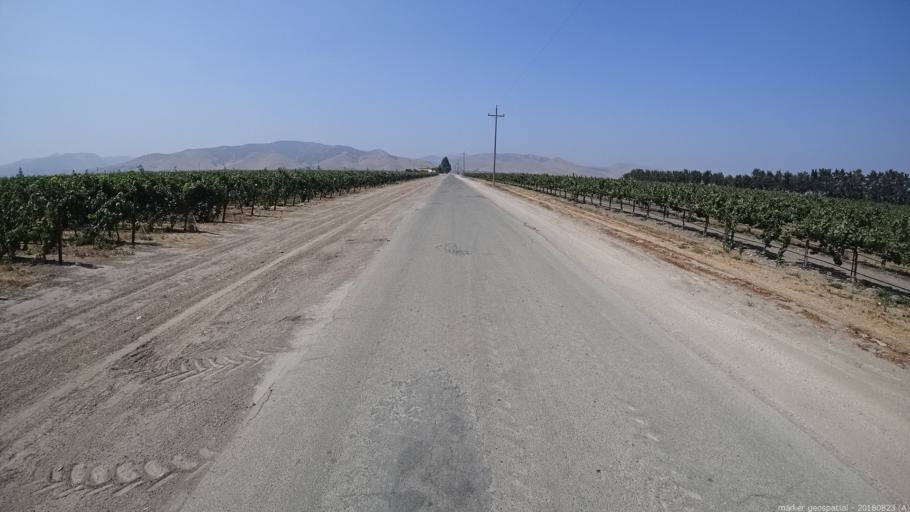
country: US
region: California
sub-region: Monterey County
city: Greenfield
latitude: 36.2699
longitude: -121.1965
